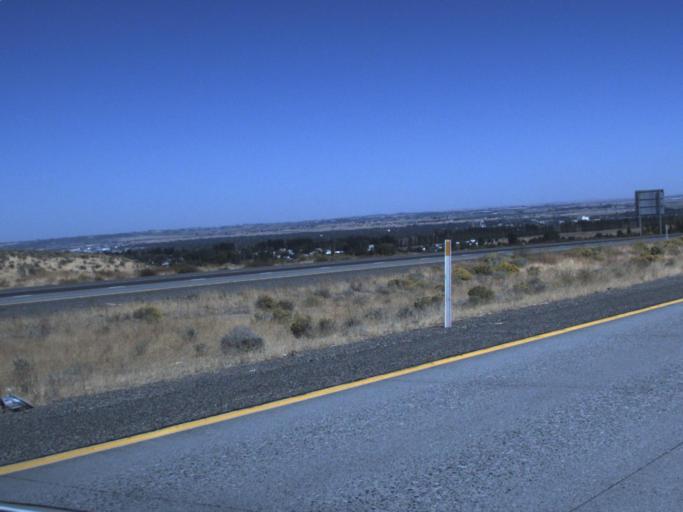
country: US
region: Washington
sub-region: Benton County
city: West Richland
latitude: 46.2456
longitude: -119.3460
